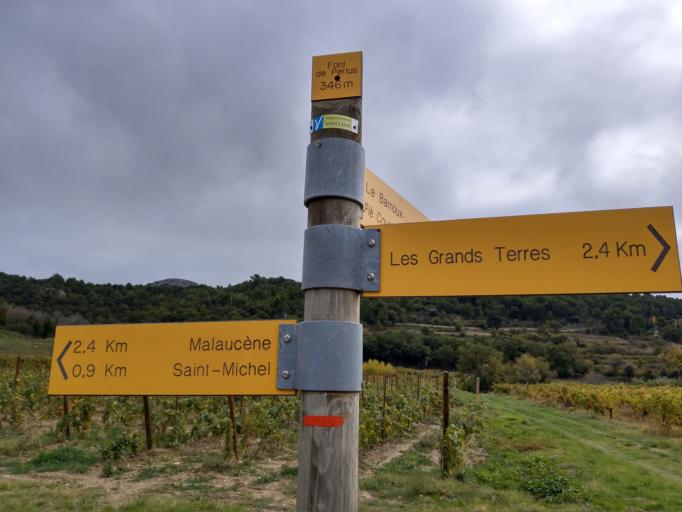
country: FR
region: Provence-Alpes-Cote d'Azur
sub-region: Departement du Vaucluse
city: Malaucene
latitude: 44.1544
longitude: 5.1196
